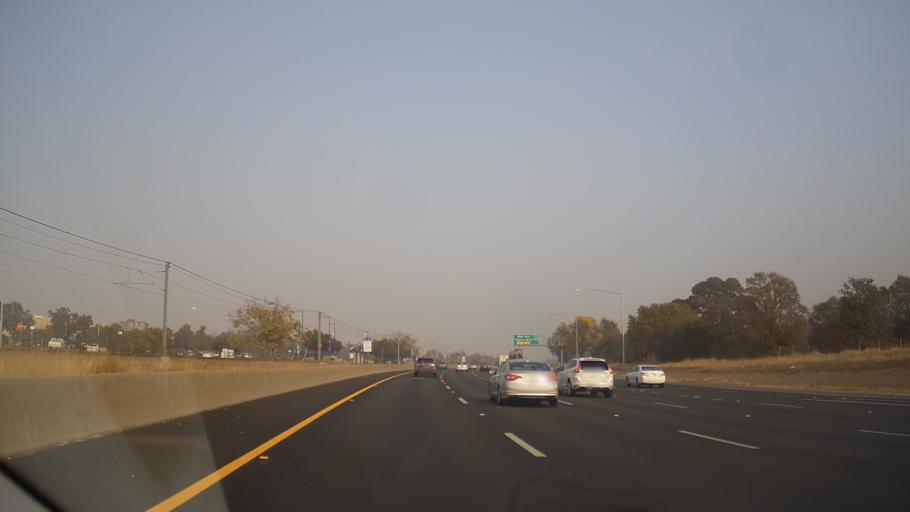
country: US
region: California
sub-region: Sacramento County
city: Arden-Arcade
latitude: 38.6417
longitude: -121.3961
